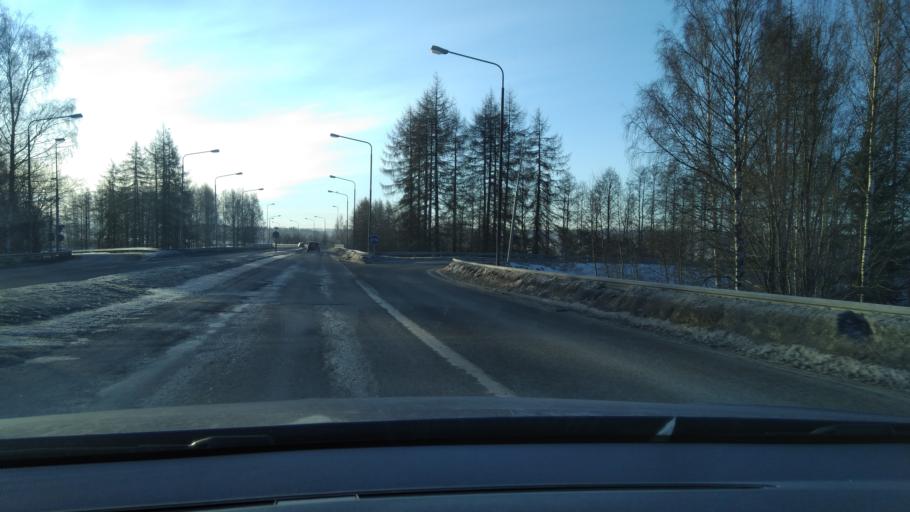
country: FI
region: Pirkanmaa
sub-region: Tampere
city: Pirkkala
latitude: 61.4988
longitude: 23.6521
